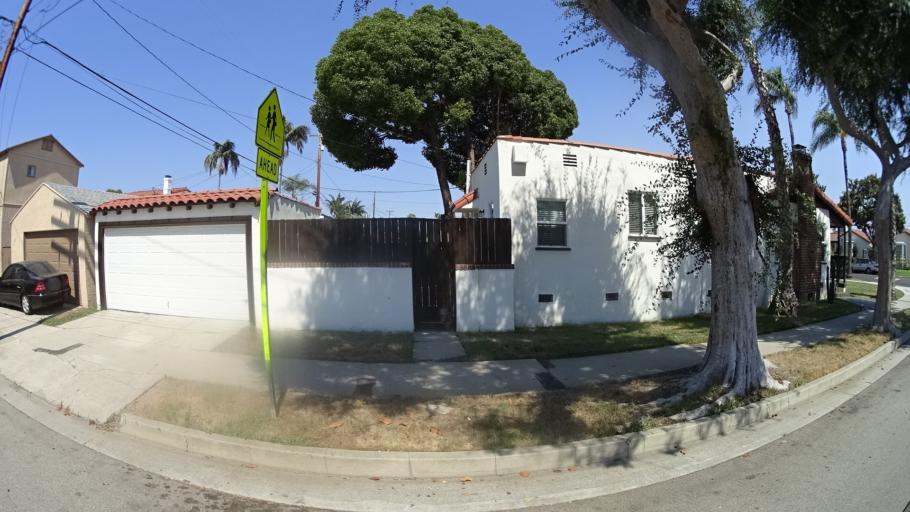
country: US
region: California
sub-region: Los Angeles County
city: Inglewood
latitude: 33.9658
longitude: -118.3221
